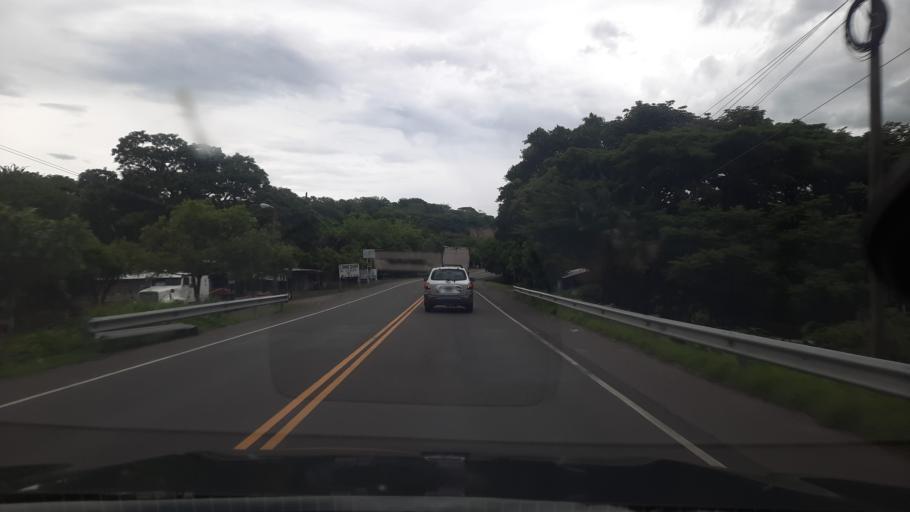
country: HN
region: Choluteca
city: Marcovia
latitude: 13.3565
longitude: -87.2732
